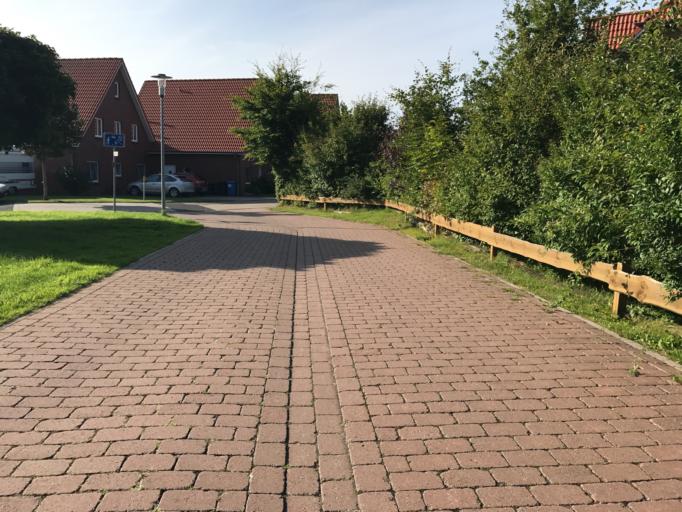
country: DE
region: Lower Saxony
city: Otterndorf
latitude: 53.8170
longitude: 8.9018
